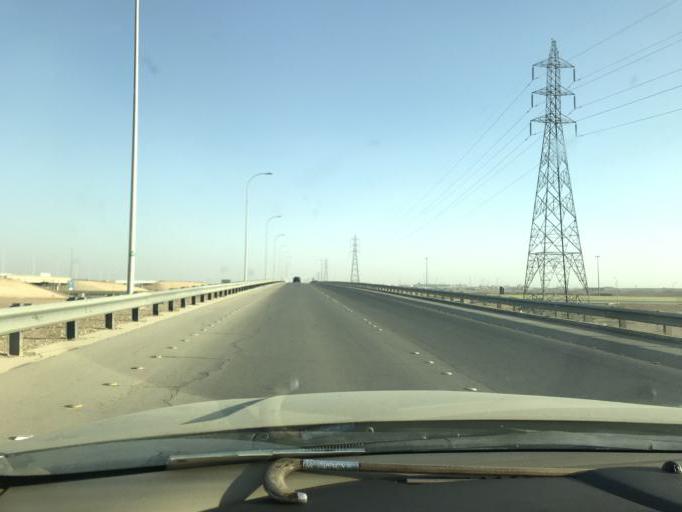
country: SA
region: Ar Riyad
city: Riyadh
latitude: 24.9048
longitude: 46.7047
